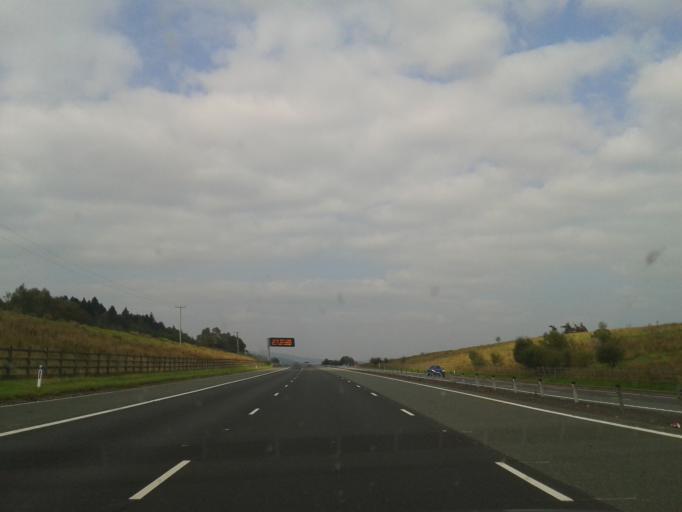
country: GB
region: Scotland
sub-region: Dumfries and Galloway
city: Moffat
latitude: 55.2809
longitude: -3.4274
